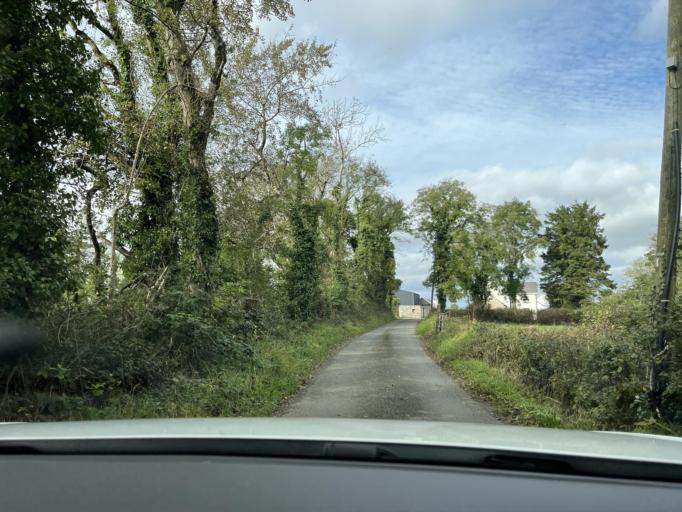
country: IE
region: Connaught
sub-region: County Leitrim
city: Carrick-on-Shannon
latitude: 53.9588
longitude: -8.0694
